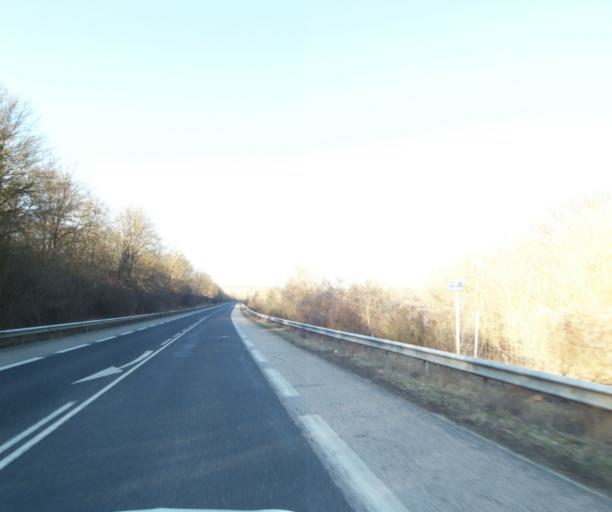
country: FR
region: Lorraine
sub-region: Departement de Meurthe-et-Moselle
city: Laxou
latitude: 48.6971
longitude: 6.1168
